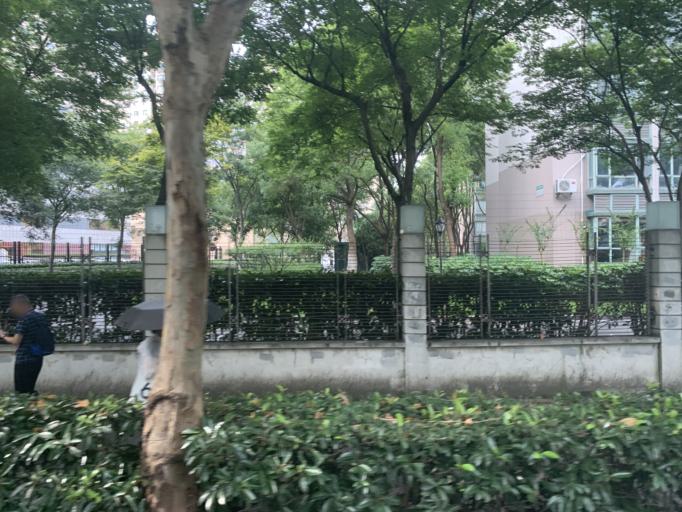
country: CN
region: Shanghai Shi
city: Huamu
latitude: 31.2138
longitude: 121.5255
